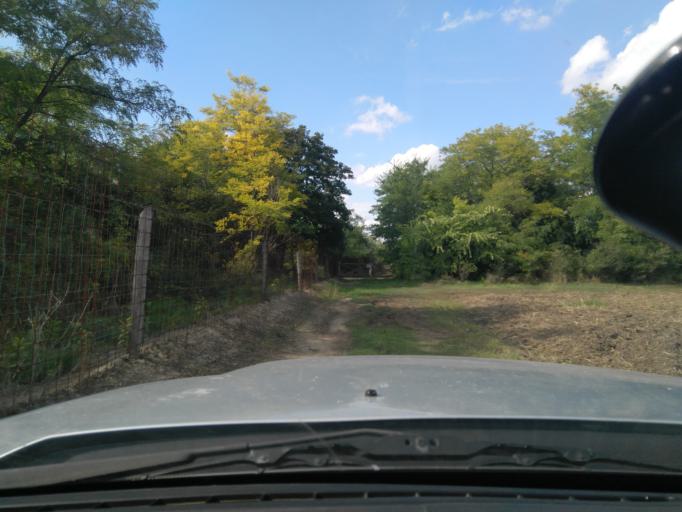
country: HU
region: Fejer
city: Bicske
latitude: 47.4586
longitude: 18.6612
